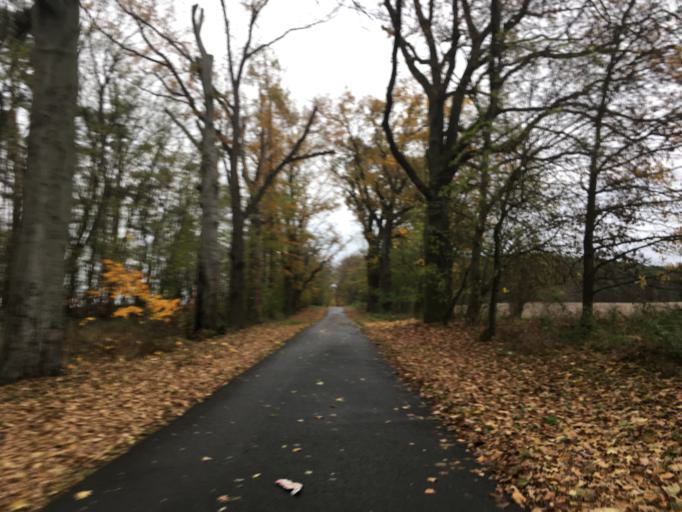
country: DE
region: Brandenburg
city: Frankfurt (Oder)
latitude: 52.2968
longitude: 14.5230
